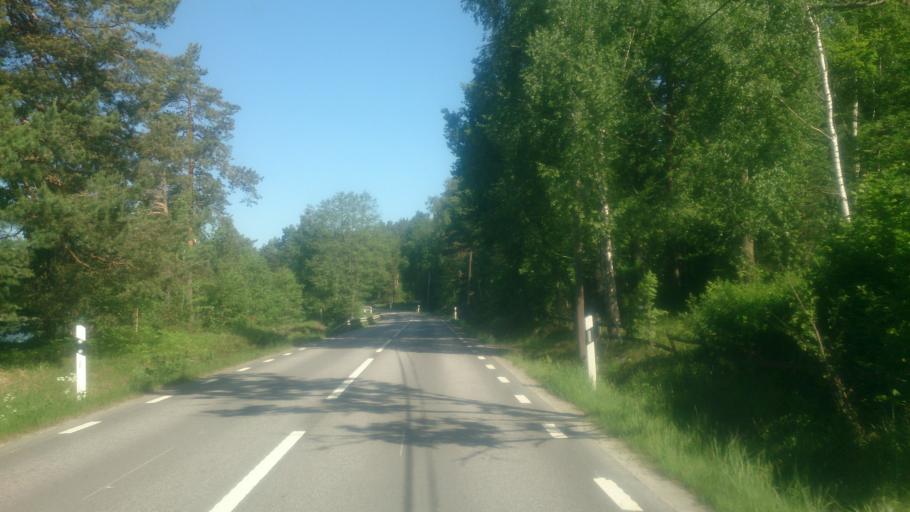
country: SE
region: OEstergoetland
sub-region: Atvidabergs Kommun
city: Atvidaberg
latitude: 58.1010
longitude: 16.1185
